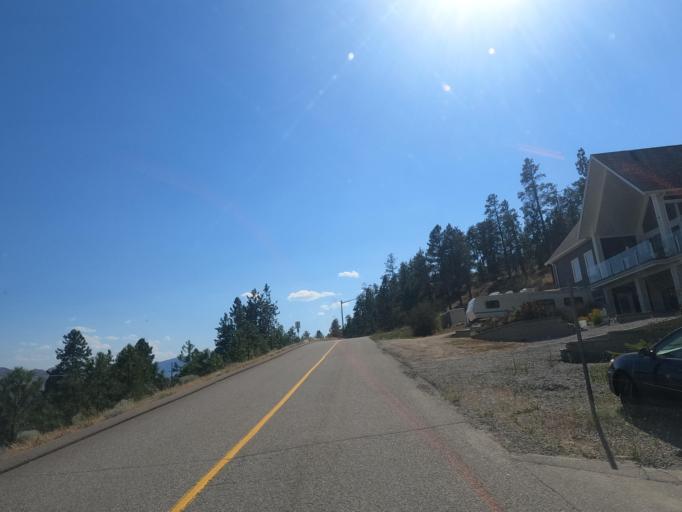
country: CA
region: British Columbia
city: Peachland
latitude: 49.7896
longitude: -119.7080
